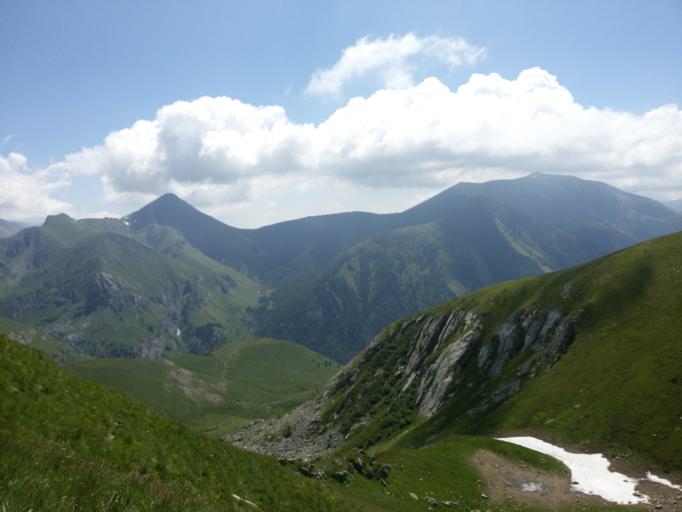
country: IT
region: Piedmont
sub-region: Provincia di Cuneo
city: Limone Piemonte
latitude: 44.1521
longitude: 7.6231
